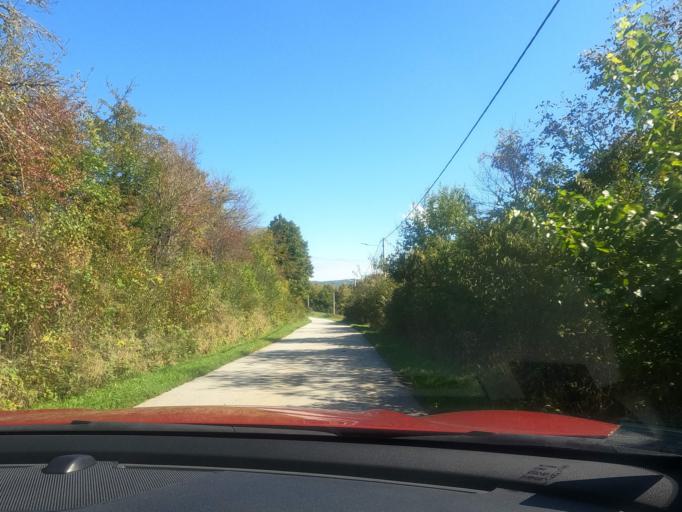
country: HR
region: Sisacko-Moslavacka
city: Petrinja
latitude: 45.3633
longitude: 16.2204
